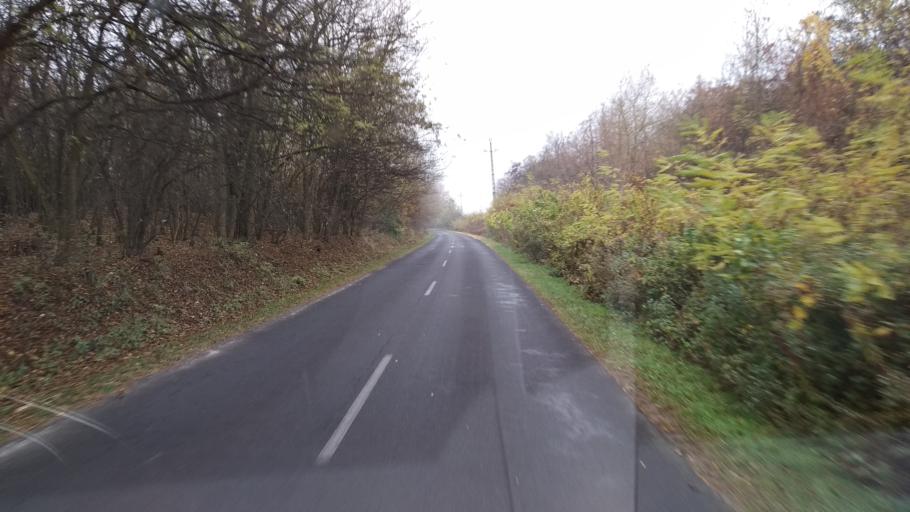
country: HU
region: Pest
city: Dunabogdany
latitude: 47.7935
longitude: 19.0720
